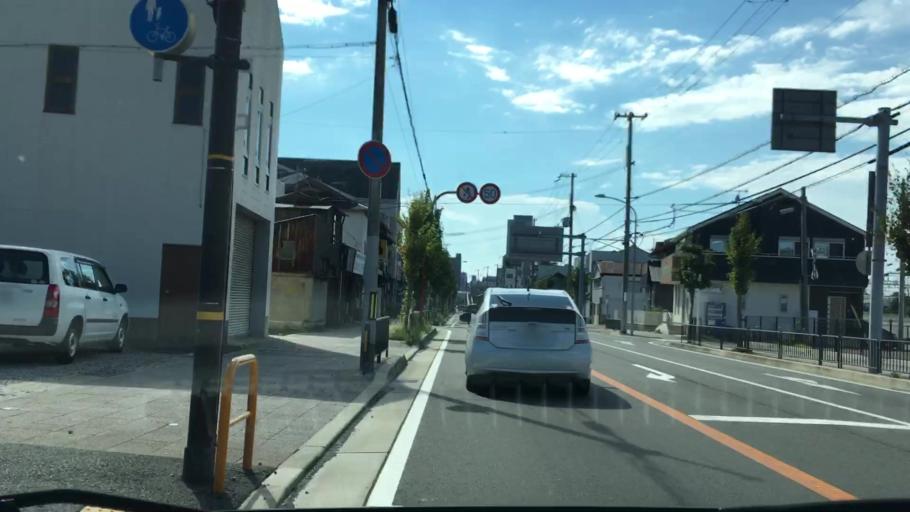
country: JP
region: Hyogo
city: Akashi
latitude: 34.6465
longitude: 135.0062
